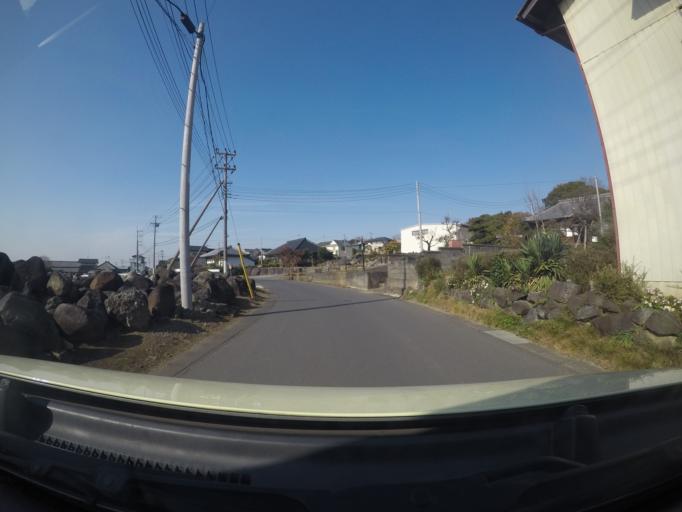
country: JP
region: Ibaraki
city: Tsukuba
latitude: 36.2055
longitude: 140.0861
